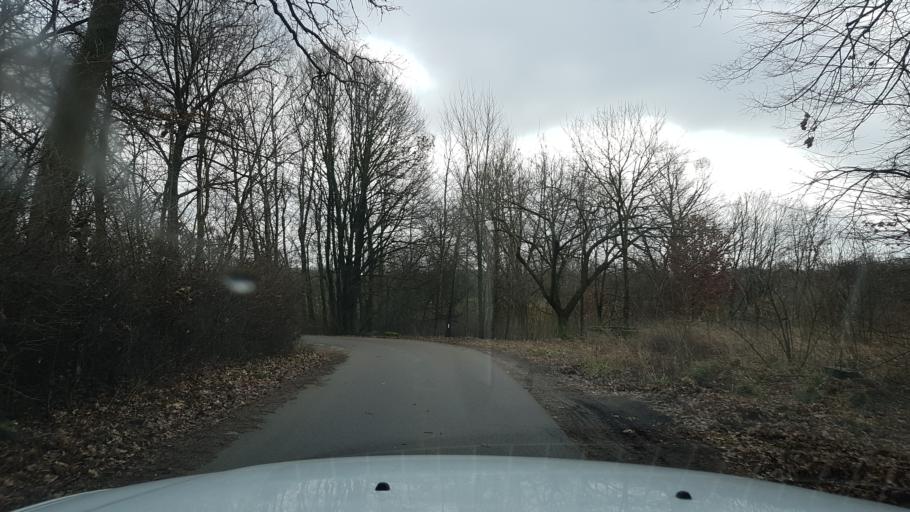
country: PL
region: West Pomeranian Voivodeship
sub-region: Powiat szczecinecki
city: Szczecinek
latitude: 53.7054
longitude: 16.7682
